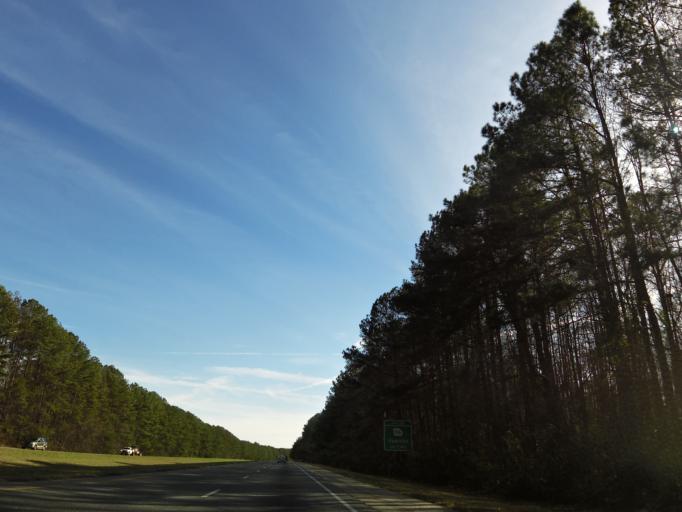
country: US
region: Georgia
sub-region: Harris County
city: Hamilton
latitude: 32.7662
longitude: -85.0194
